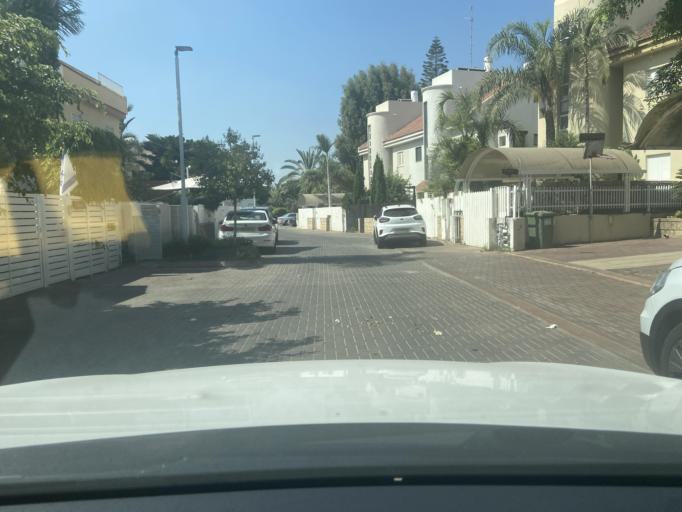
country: IL
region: Central District
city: Yehud
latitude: 32.0317
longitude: 34.8812
